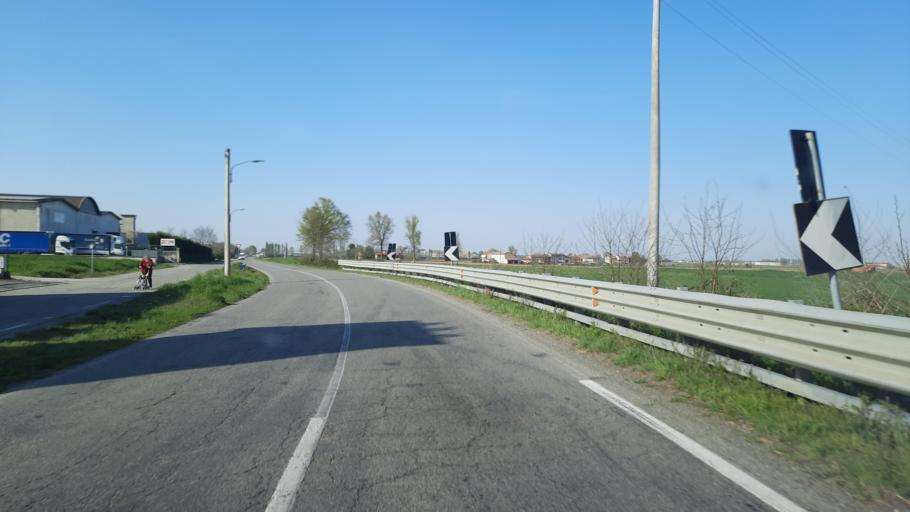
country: IT
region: Piedmont
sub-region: Provincia di Alessandria
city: Terruggia
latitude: 45.0657
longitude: 8.4676
